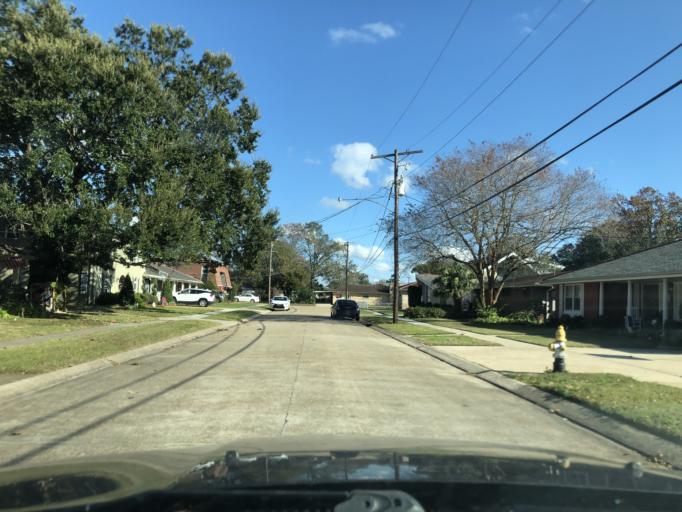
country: US
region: Louisiana
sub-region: Jefferson Parish
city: Metairie Terrace
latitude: 29.9874
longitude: -90.1625
